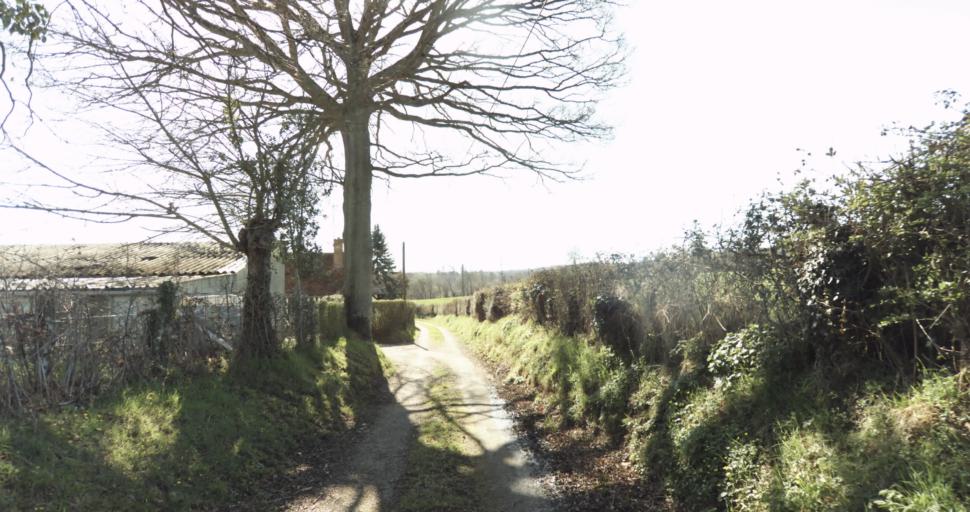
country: FR
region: Lower Normandy
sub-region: Departement du Calvados
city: Livarot
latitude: 48.9879
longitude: 0.0731
